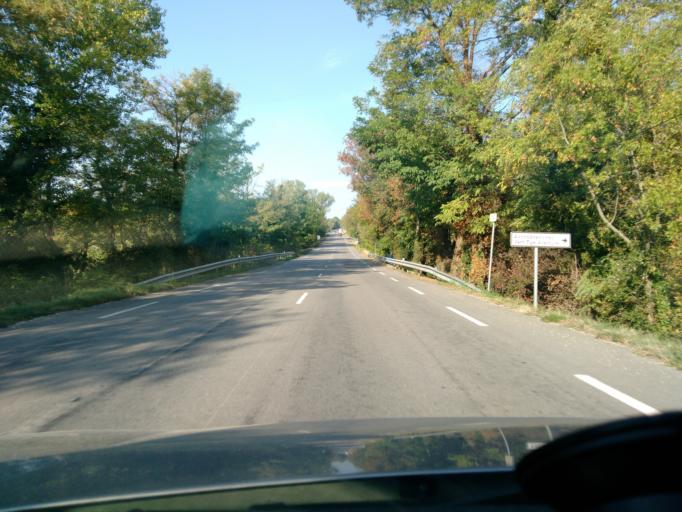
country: FR
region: Rhone-Alpes
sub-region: Departement de la Drome
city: La Garde-Adhemar
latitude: 44.4200
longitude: 4.7847
